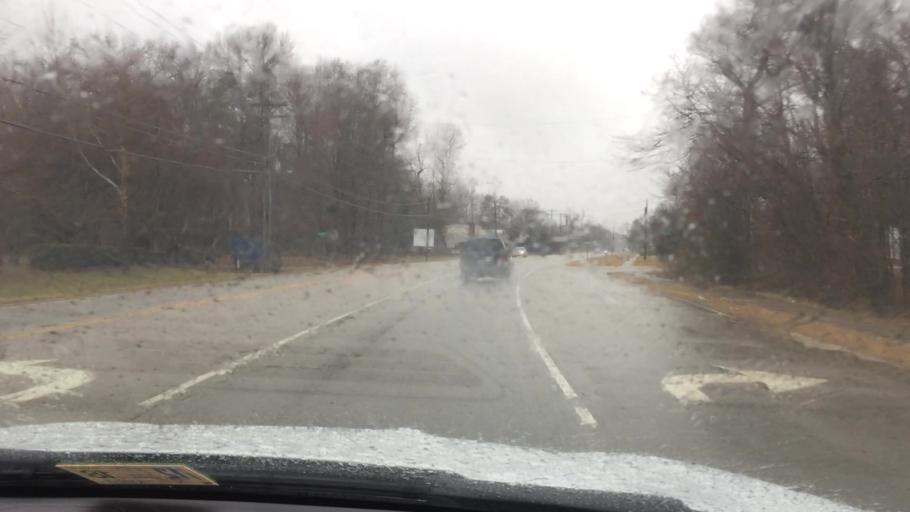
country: US
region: Virginia
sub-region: City of Williamsburg
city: Williamsburg
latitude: 37.2204
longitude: -76.6256
